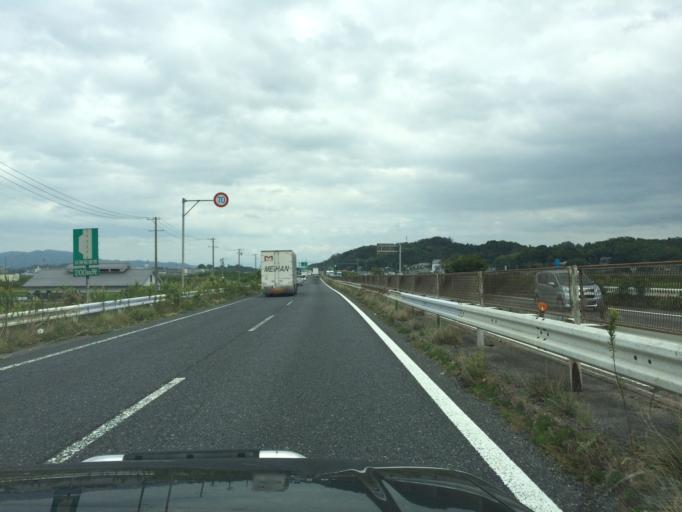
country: JP
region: Mie
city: Ueno-ebisumachi
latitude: 34.7420
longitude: 136.1156
